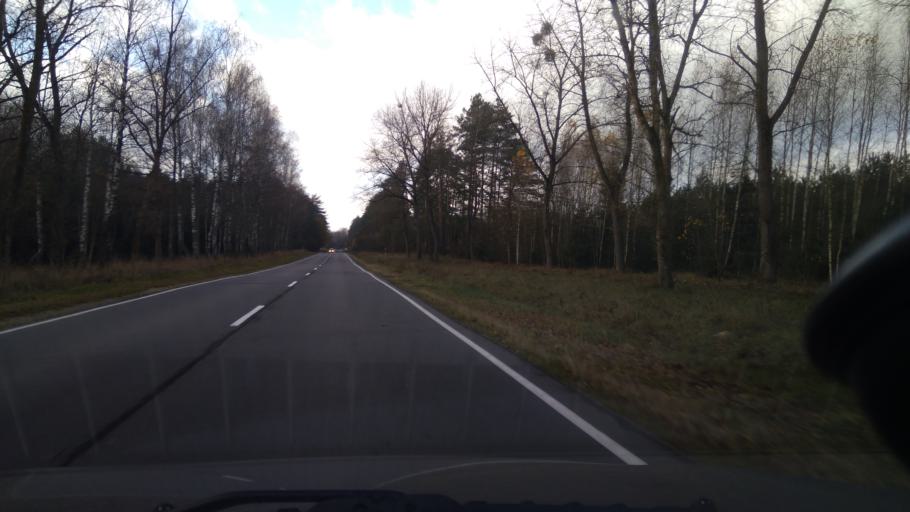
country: BY
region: Minsk
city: Slutsk
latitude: 53.2317
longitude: 27.6507
